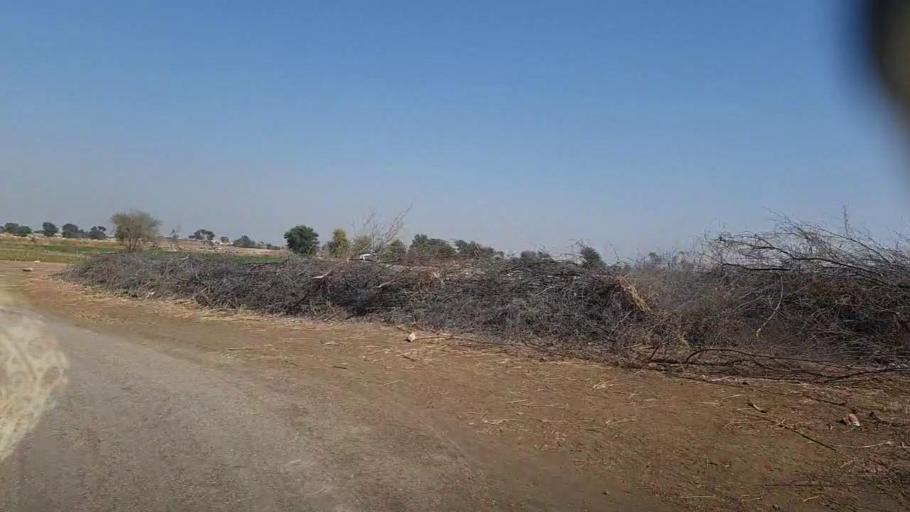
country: PK
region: Sindh
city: Khairpur
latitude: 27.9780
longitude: 69.8483
